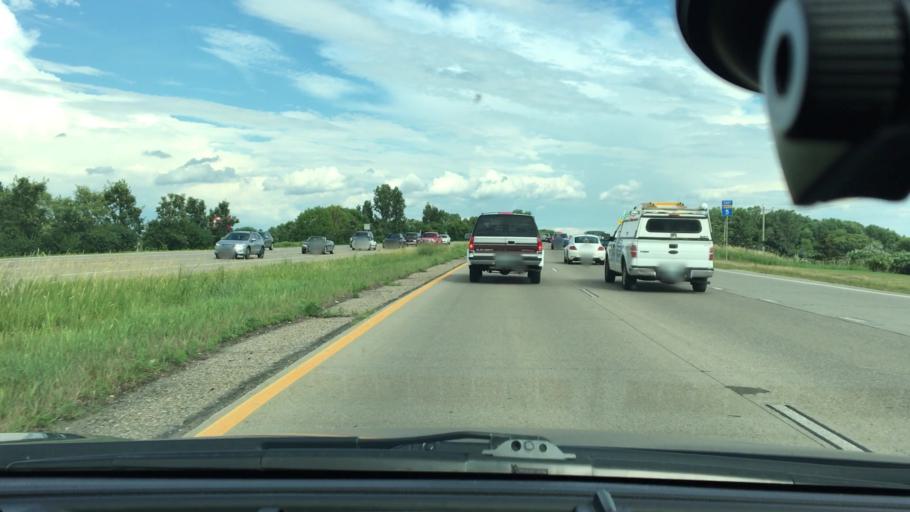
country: US
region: Minnesota
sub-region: Carver County
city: Chanhassen
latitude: 44.8614
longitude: -93.5469
